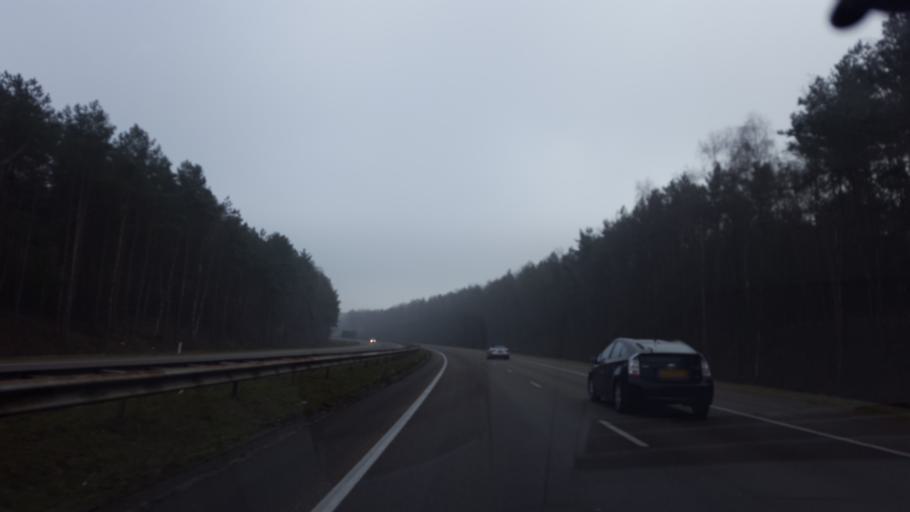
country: NL
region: Limburg
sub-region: Gemeente Leudal
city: Haelen
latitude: 51.2047
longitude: 5.9242
